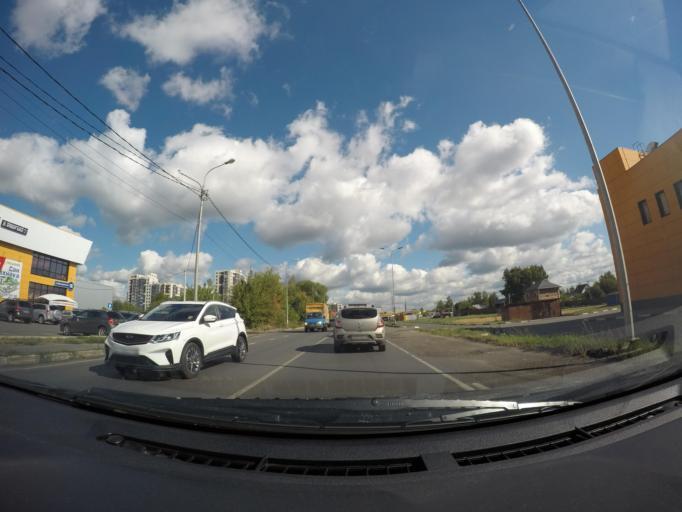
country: RU
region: Moskovskaya
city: Ramenskoye
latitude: 55.5864
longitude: 38.2487
